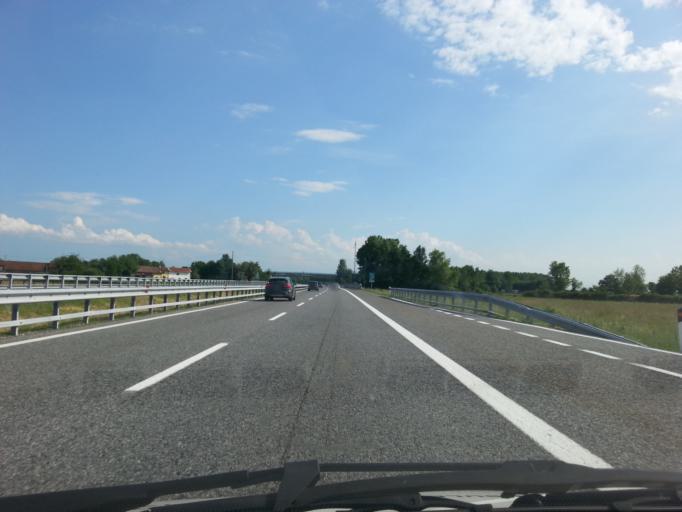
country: IT
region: Piedmont
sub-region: Provincia di Cuneo
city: Caramagna Piemonte
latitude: 44.7547
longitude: 7.7499
